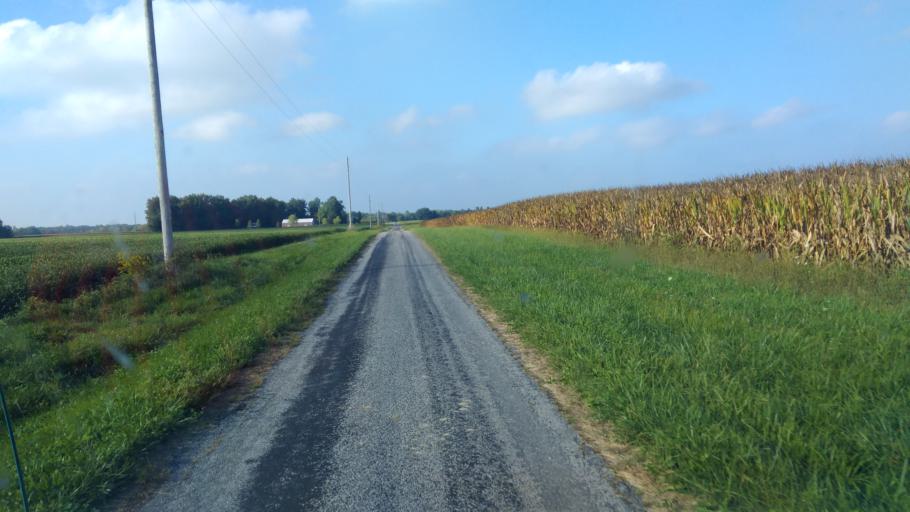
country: US
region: Ohio
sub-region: Wyandot County
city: Upper Sandusky
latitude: 40.7606
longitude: -83.3622
